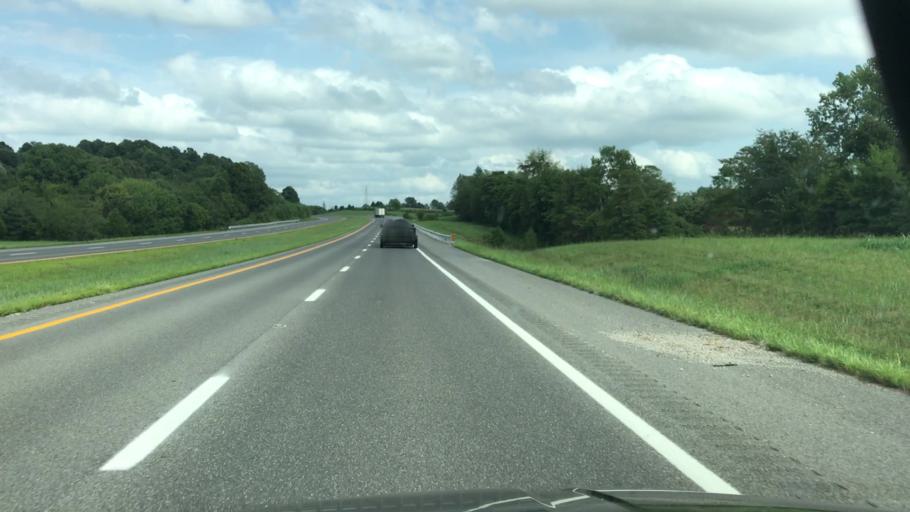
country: US
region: Kentucky
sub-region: Caldwell County
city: Princeton
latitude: 37.1101
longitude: -87.9562
